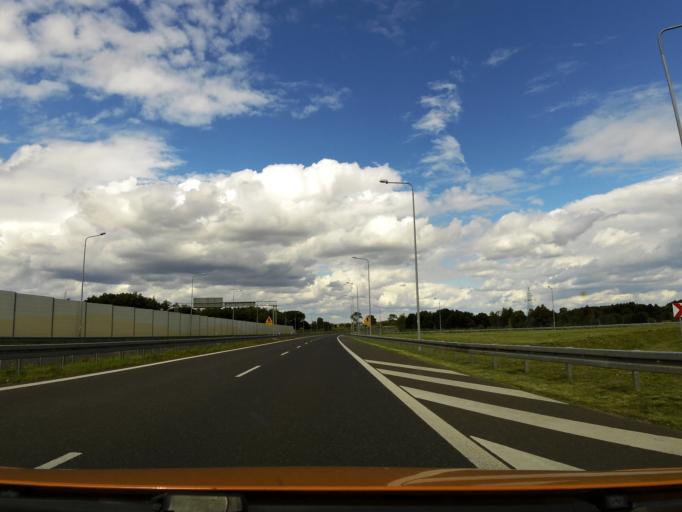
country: PL
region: West Pomeranian Voivodeship
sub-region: Powiat goleniowski
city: Nowogard
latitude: 53.6859
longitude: 15.0894
